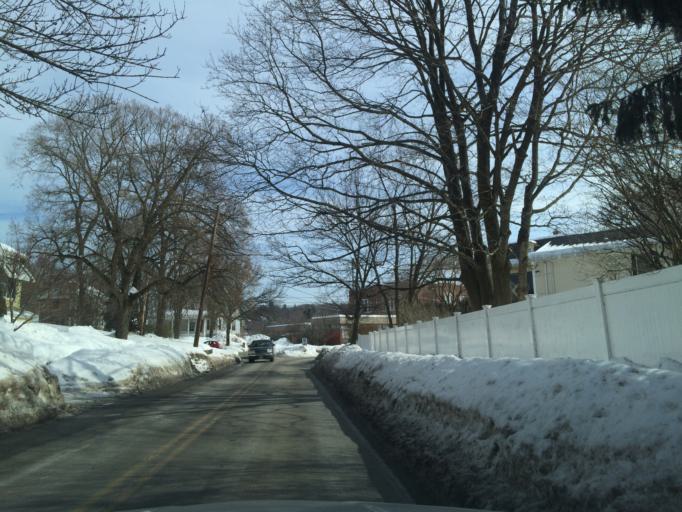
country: US
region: Massachusetts
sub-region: Middlesex County
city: Newton
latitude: 42.3517
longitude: -71.2272
